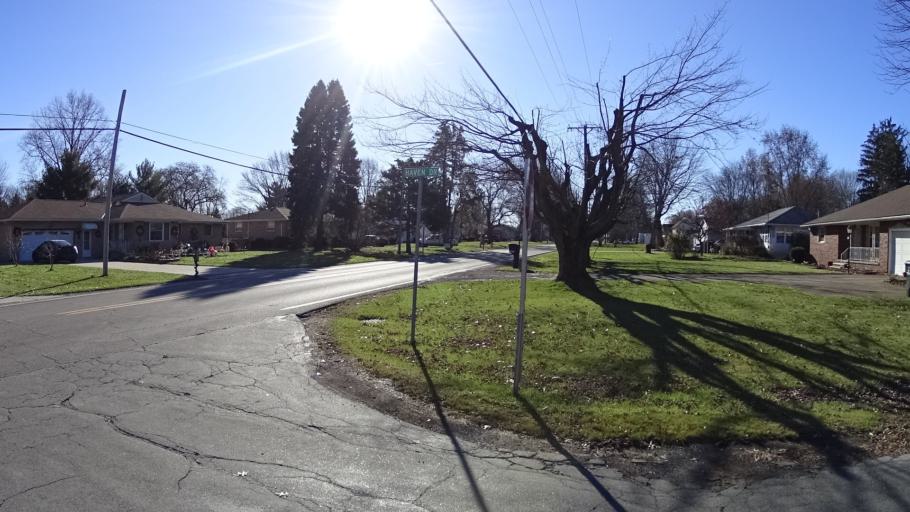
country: US
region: Ohio
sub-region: Lorain County
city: Elyria
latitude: 41.3991
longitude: -82.1498
